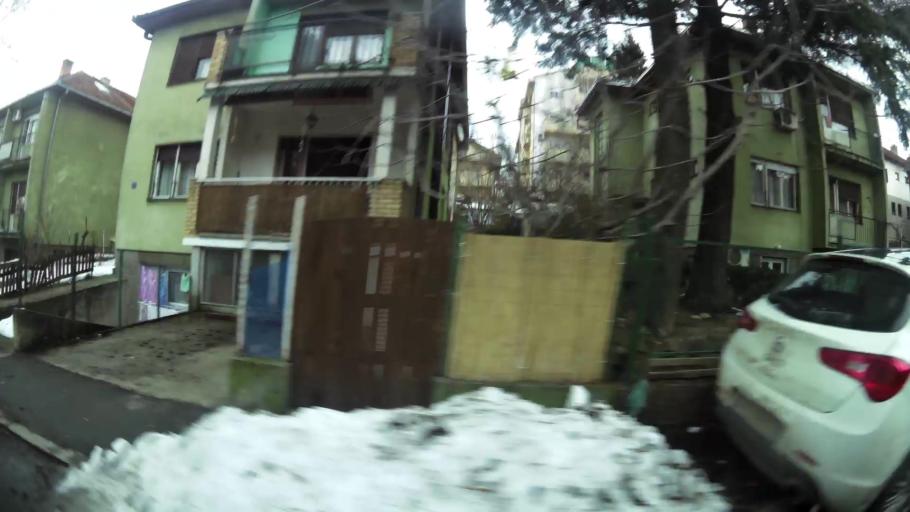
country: RS
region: Central Serbia
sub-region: Belgrade
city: Rakovica
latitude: 44.7532
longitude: 20.4166
